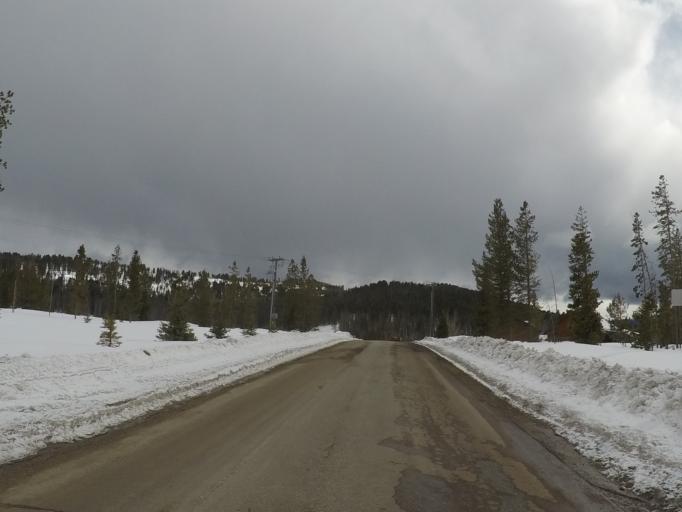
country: US
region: Montana
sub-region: Granite County
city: Philipsburg
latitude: 46.2009
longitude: -113.2526
